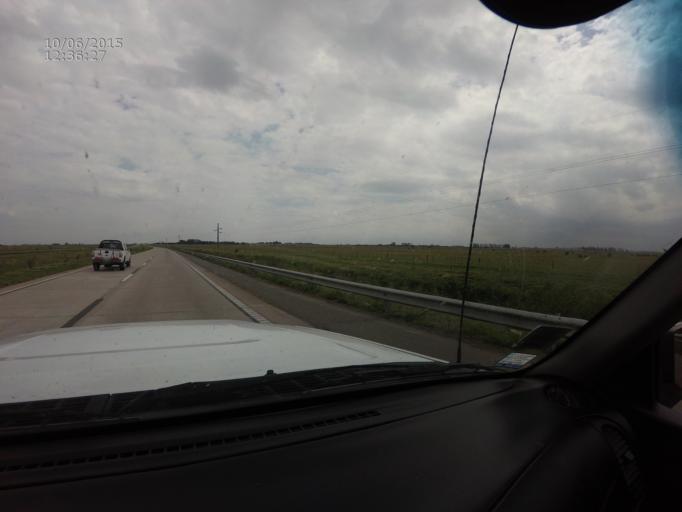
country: AR
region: Santa Fe
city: Carcarana
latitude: -32.8710
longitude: -61.1987
